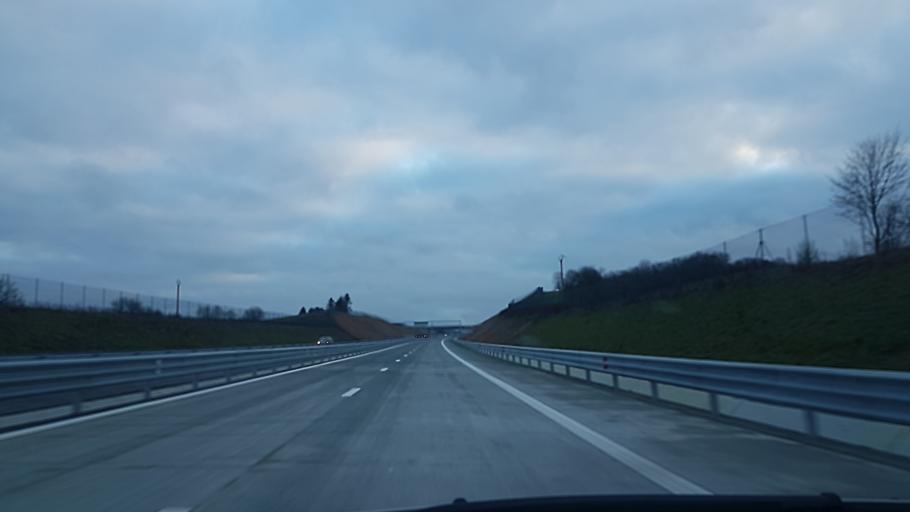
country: FR
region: Champagne-Ardenne
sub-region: Departement des Ardennes
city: Rocroi
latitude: 49.9723
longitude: 4.5380
